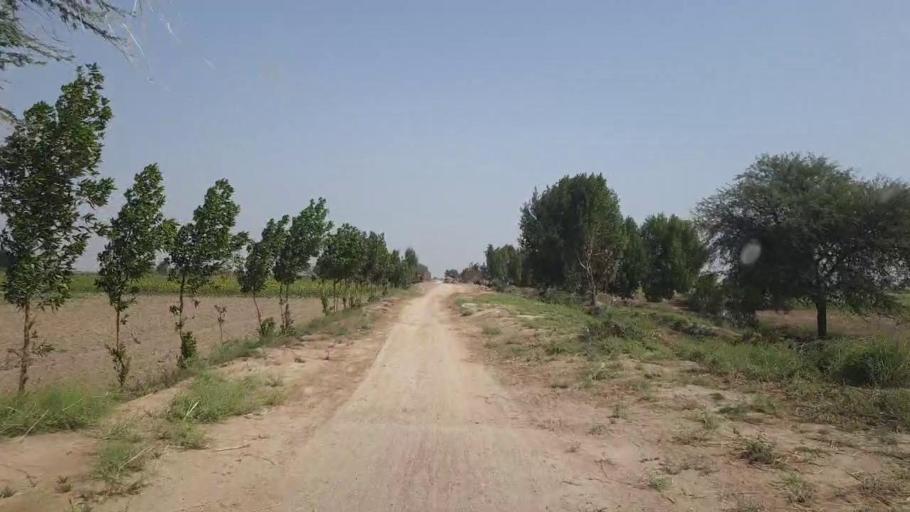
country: PK
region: Sindh
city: Badin
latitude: 24.4774
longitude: 68.5724
